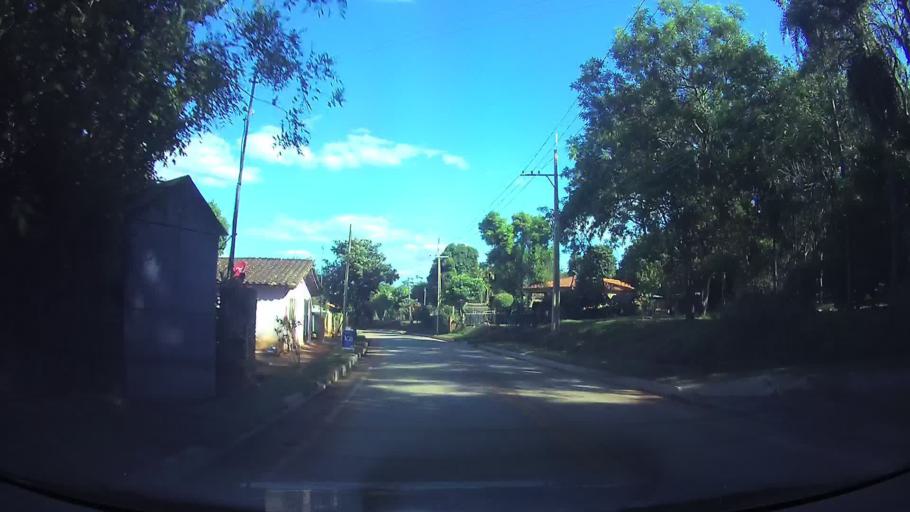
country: PY
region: Cordillera
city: Caacupe
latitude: -25.3715
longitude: -57.1405
